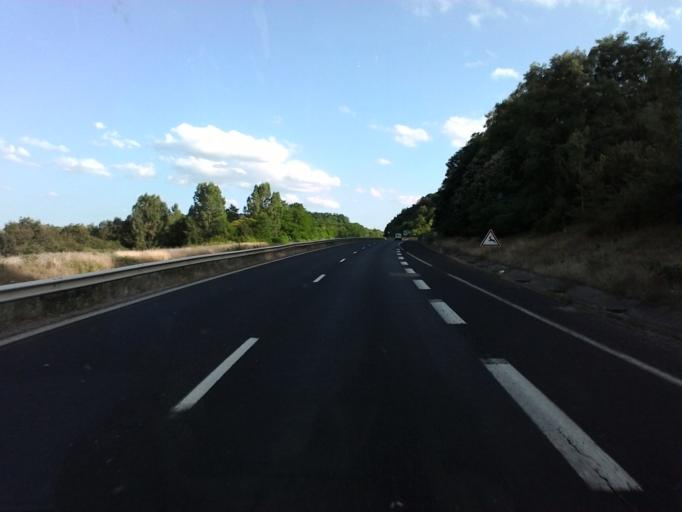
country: FR
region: Lorraine
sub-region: Departement de Meurthe-et-Moselle
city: Flavigny-sur-Moselle
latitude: 48.5733
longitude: 6.1748
